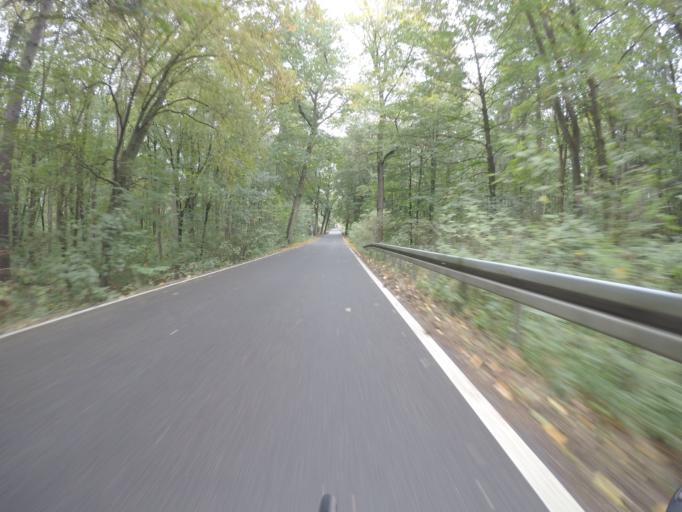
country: DE
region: Brandenburg
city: Strausberg
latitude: 52.6069
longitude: 13.9023
